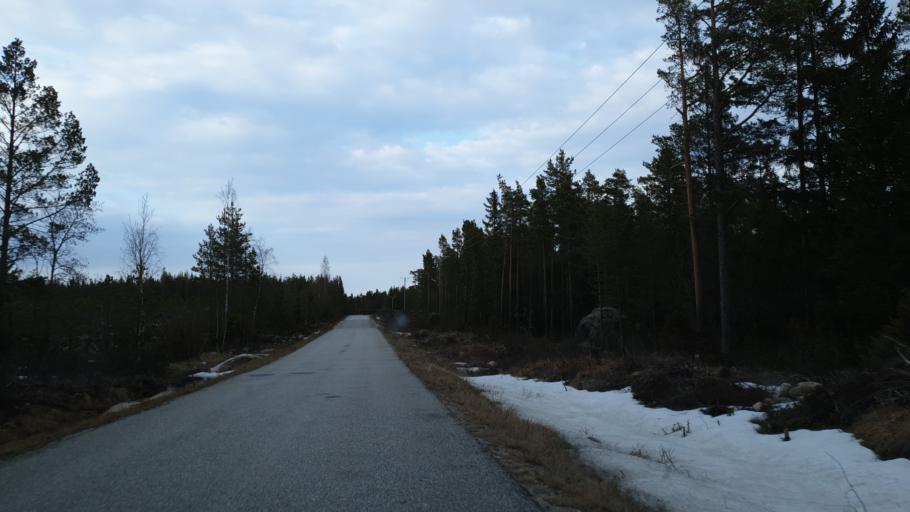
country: SE
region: Vaesternorrland
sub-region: Sundsvalls Kommun
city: Njurundabommen
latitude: 61.9941
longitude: 17.3834
